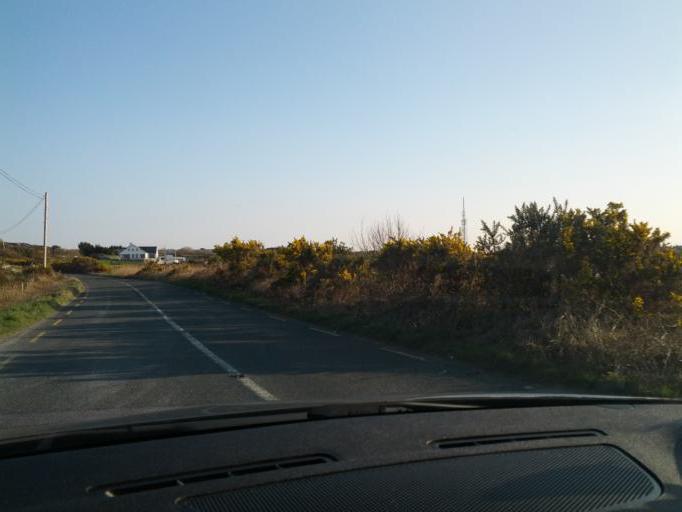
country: IE
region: Connaught
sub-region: County Galway
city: Oughterard
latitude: 53.2975
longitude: -9.5508
